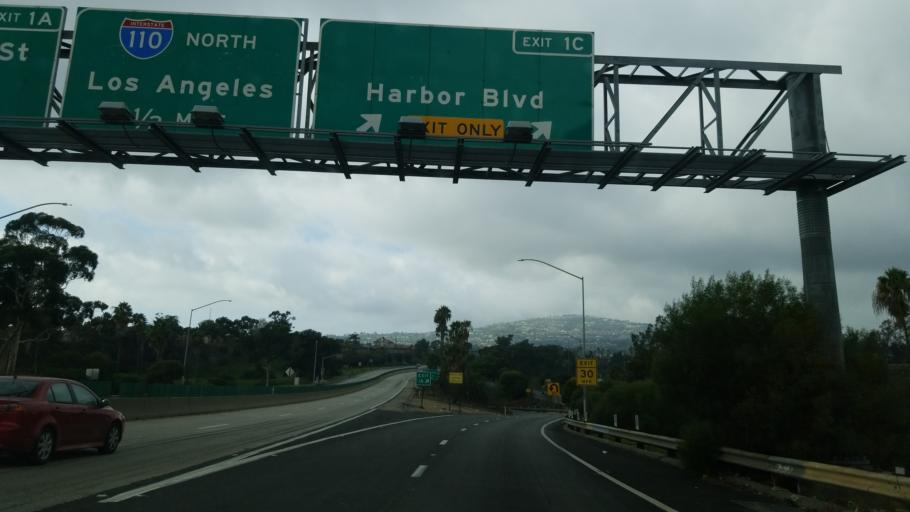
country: US
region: California
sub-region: Los Angeles County
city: San Pedro
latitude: 33.7496
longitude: -118.2814
